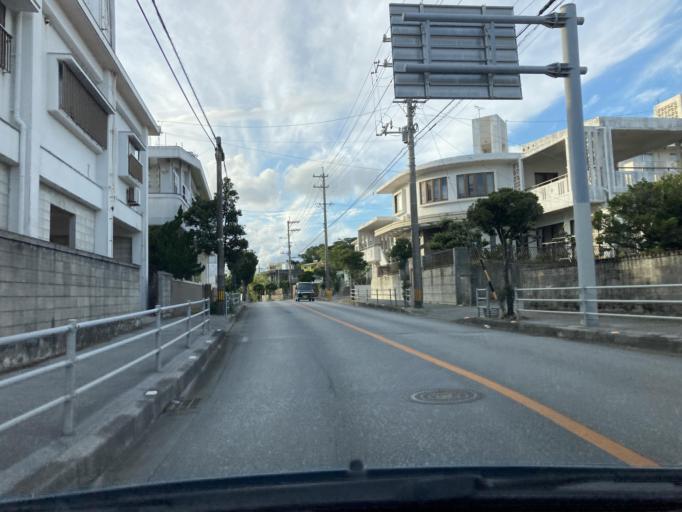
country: JP
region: Okinawa
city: Tomigusuku
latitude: 26.1504
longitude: 127.7090
